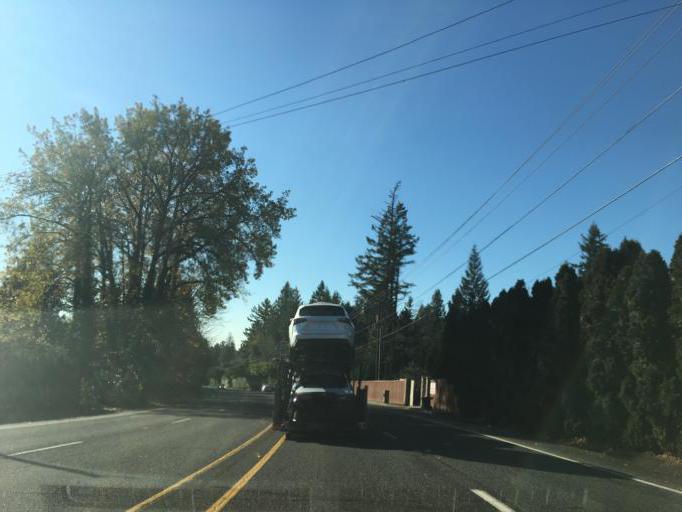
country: US
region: Oregon
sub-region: Washington County
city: West Slope
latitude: 45.5016
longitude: -122.7523
